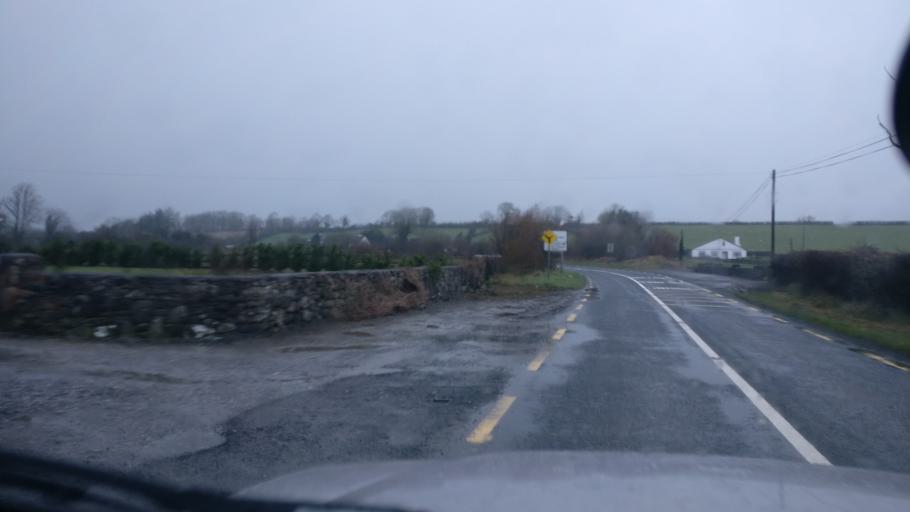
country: IE
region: Connaught
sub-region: County Galway
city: Loughrea
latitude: 53.1603
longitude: -8.4866
